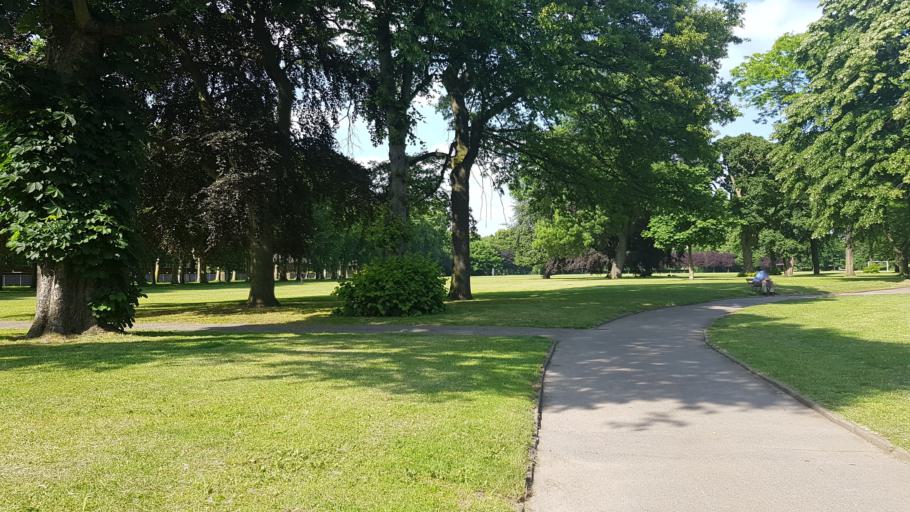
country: GB
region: England
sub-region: Greater London
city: Hackney
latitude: 51.5384
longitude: -0.0394
